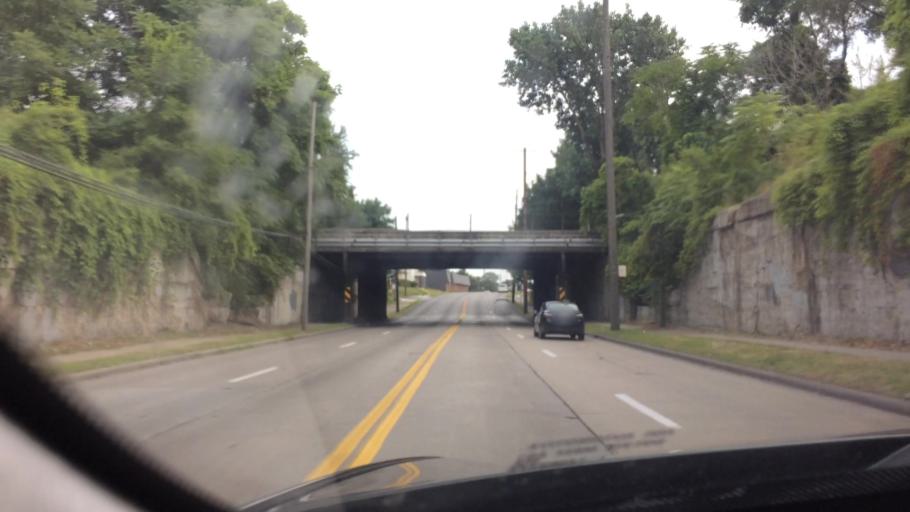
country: US
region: Ohio
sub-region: Wood County
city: Rossford
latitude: 41.6371
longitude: -83.5910
